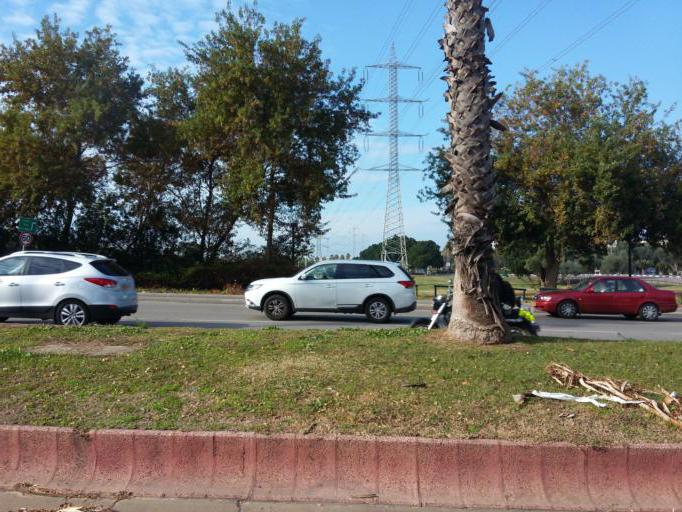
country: IL
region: Tel Aviv
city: Tel Aviv
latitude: 32.0971
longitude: 34.7935
